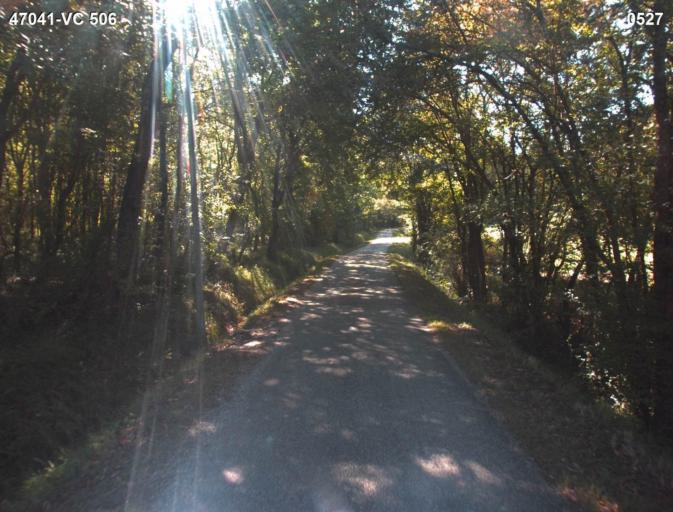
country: FR
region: Aquitaine
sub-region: Departement du Lot-et-Garonne
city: Port-Sainte-Marie
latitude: 44.2089
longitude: 0.3850
